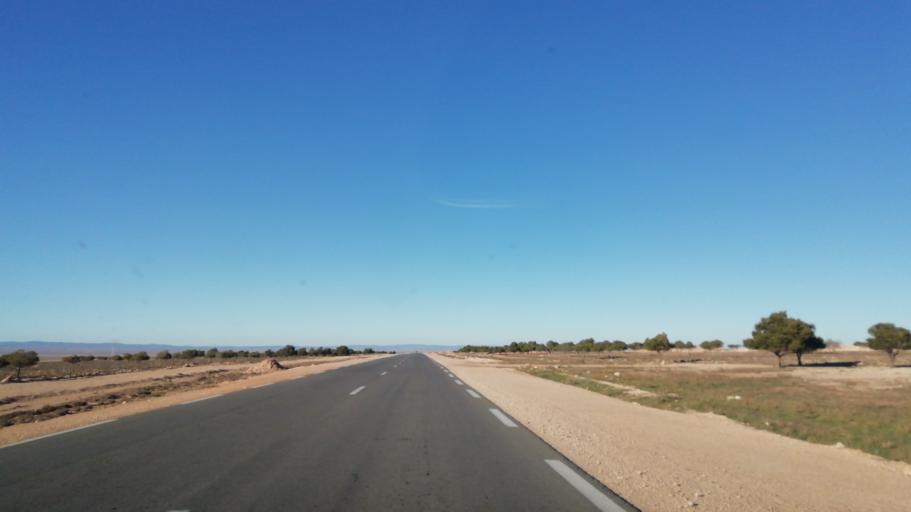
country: DZ
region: Tlemcen
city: Sebdou
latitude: 34.2831
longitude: -1.2593
